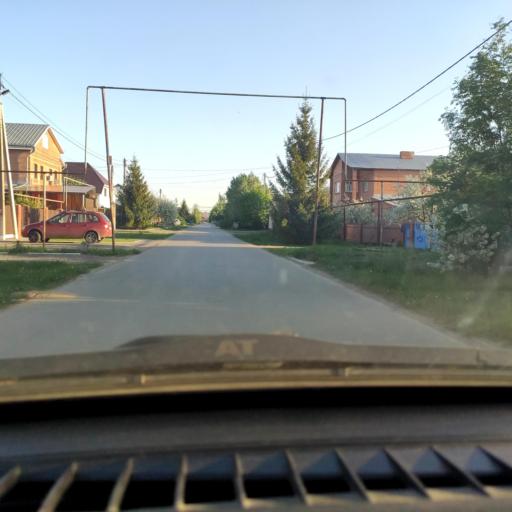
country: RU
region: Samara
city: Tol'yatti
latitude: 53.5617
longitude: 49.4026
